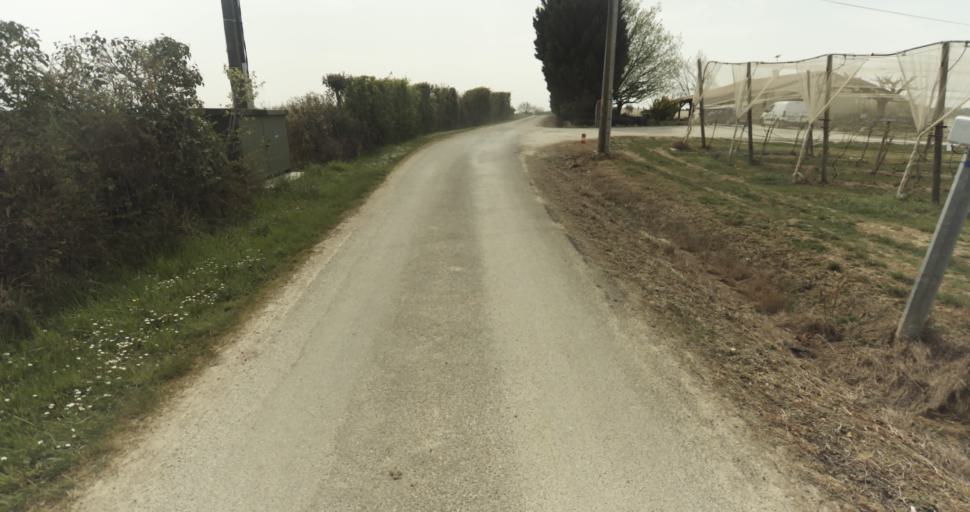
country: FR
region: Midi-Pyrenees
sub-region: Departement du Tarn-et-Garonne
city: Moissac
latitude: 44.1198
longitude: 1.0545
